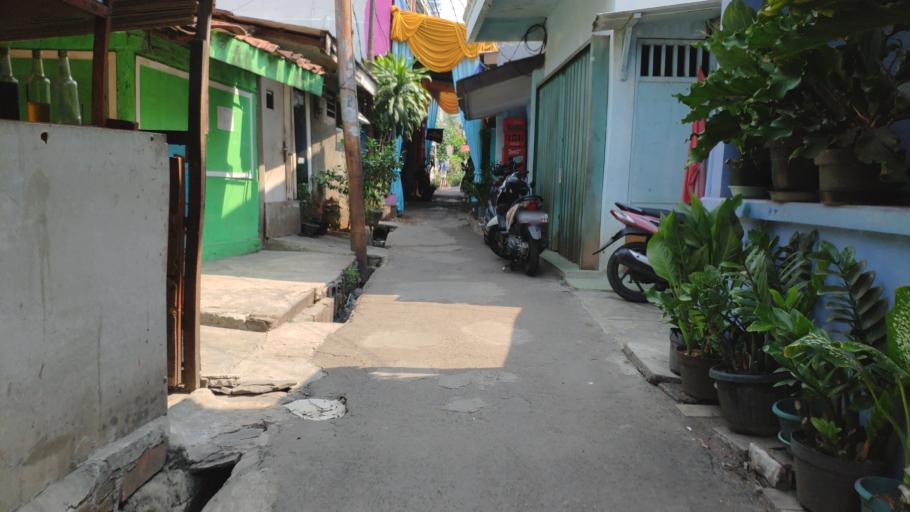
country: ID
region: Jakarta Raya
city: Jakarta
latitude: -6.2534
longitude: 106.8117
